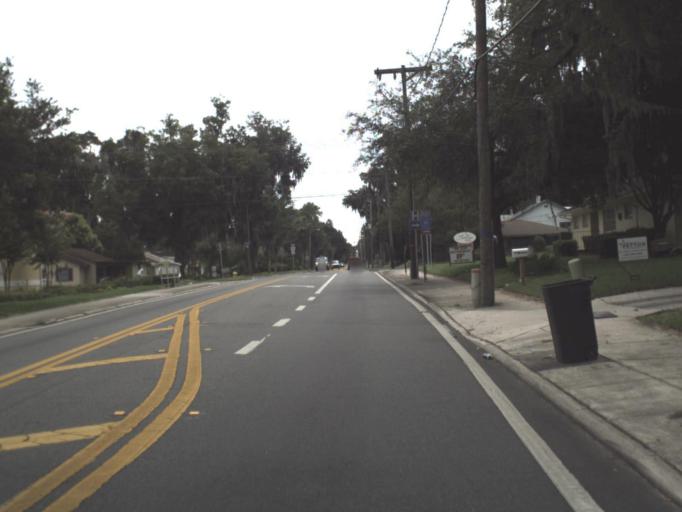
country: US
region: Florida
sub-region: Pasco County
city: Dade City
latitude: 28.3646
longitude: -82.2007
